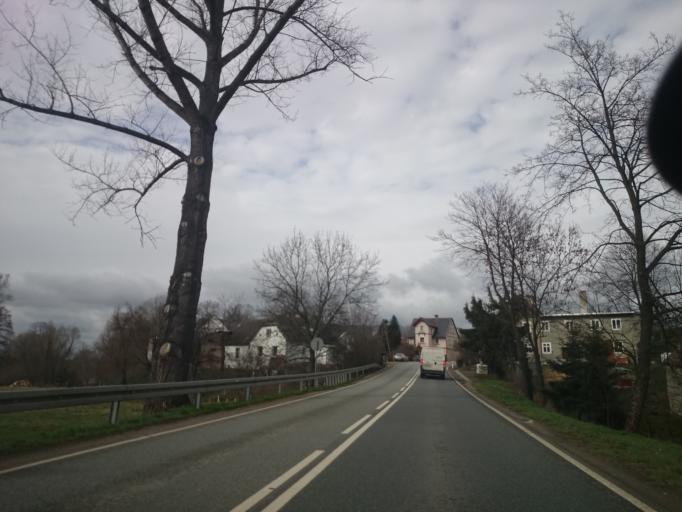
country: PL
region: Lower Silesian Voivodeship
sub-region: Powiat klodzki
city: Bystrzyca Klodzka
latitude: 50.3204
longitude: 16.6604
